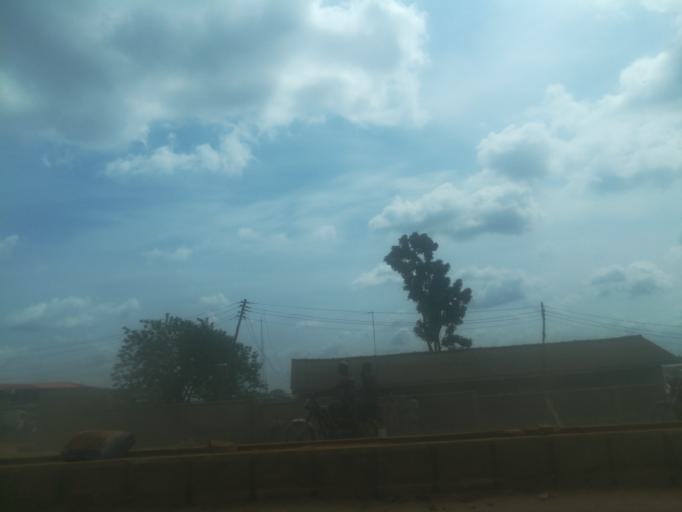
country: NG
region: Oyo
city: Ibadan
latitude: 7.4038
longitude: 3.9290
